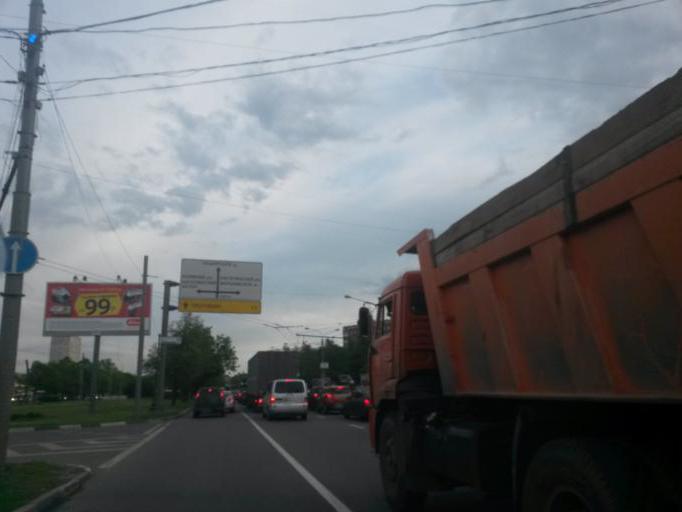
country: RU
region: Moskovskaya
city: Kozhukhovo
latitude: 55.6800
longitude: 37.6639
